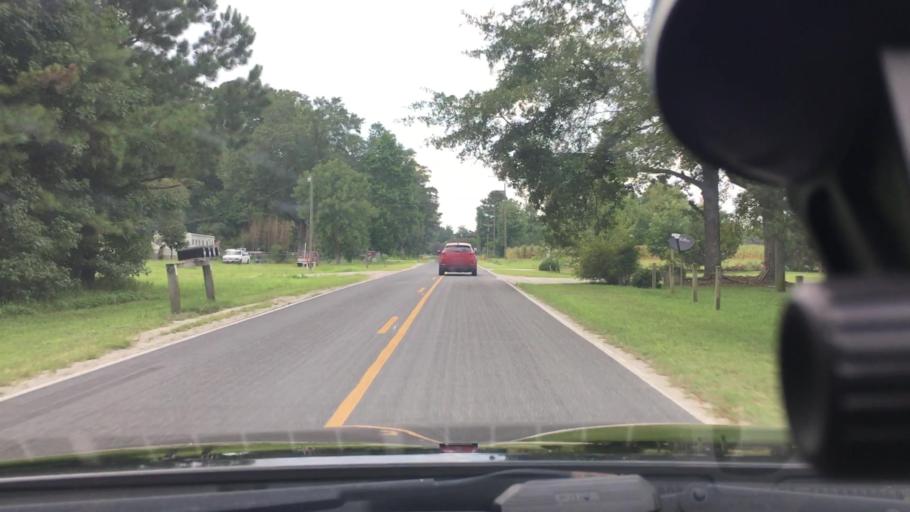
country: US
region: North Carolina
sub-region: Craven County
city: New Bern
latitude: 35.1760
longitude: -77.0531
